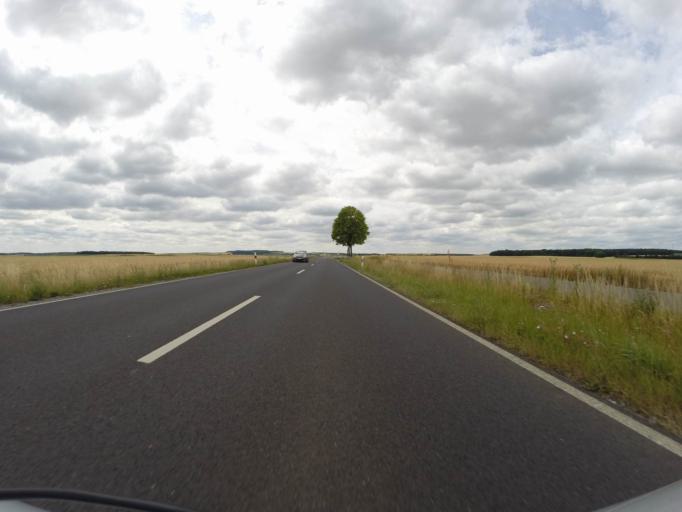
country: DE
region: Bavaria
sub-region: Regierungsbezirk Unterfranken
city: Kolitzheim
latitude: 49.9334
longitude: 10.2535
